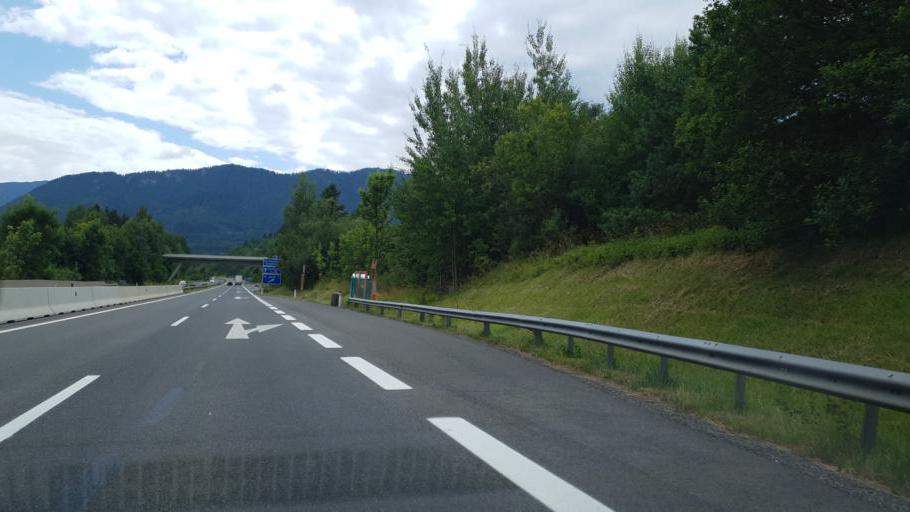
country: AT
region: Carinthia
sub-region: Politischer Bezirk Villach Land
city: Rosegg
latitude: 46.5632
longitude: 14.0063
